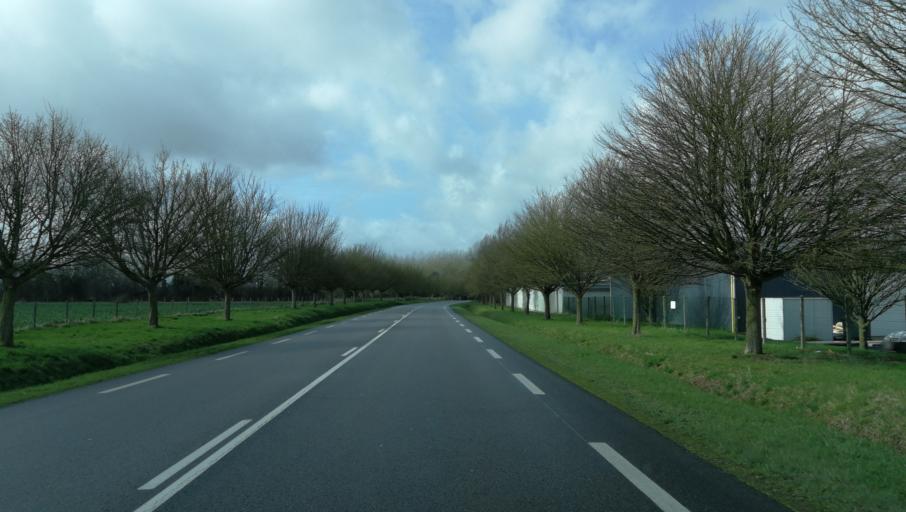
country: FR
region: Haute-Normandie
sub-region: Departement de l'Eure
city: Epaignes
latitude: 49.2737
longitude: 0.4452
